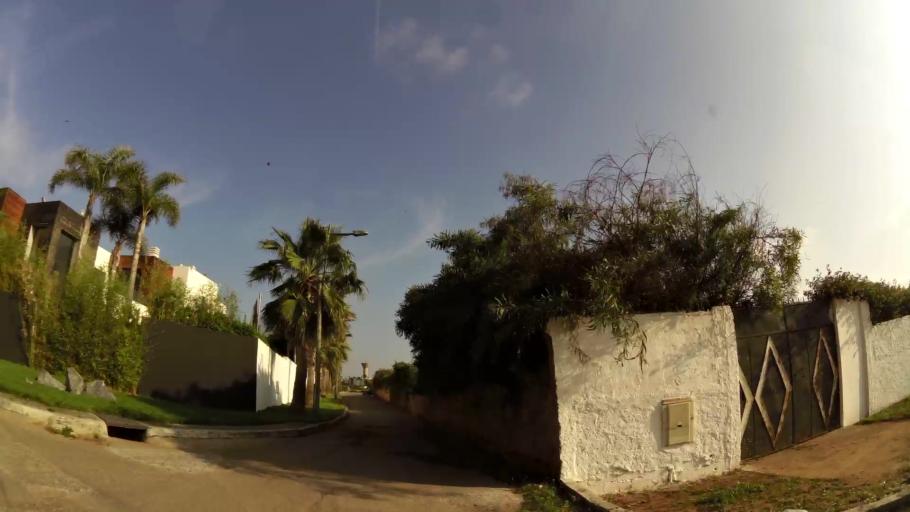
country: MA
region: Rabat-Sale-Zemmour-Zaer
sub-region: Rabat
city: Rabat
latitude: 33.9414
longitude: -6.8159
